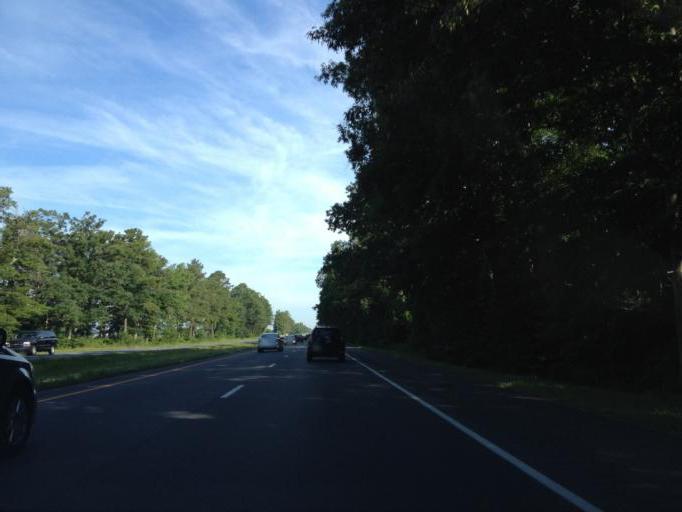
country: US
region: Delaware
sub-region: Sussex County
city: Millsboro
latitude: 38.6075
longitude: -75.3251
